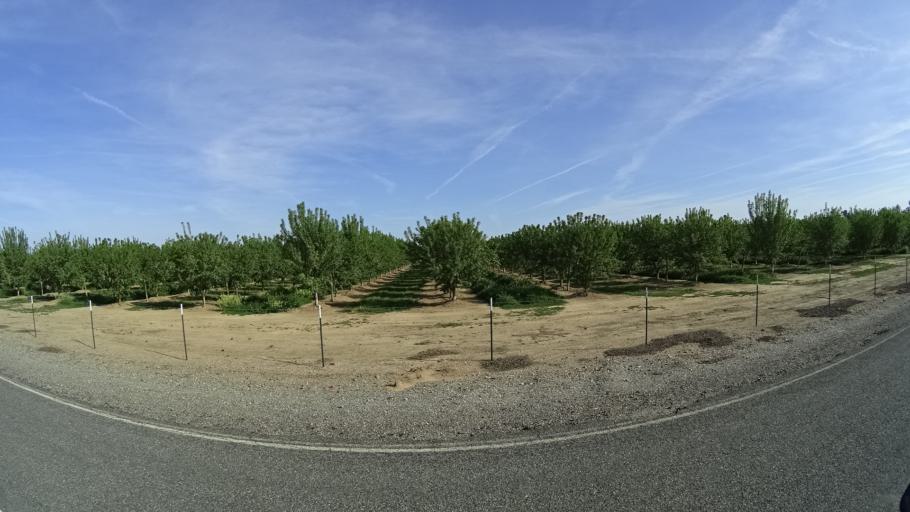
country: US
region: California
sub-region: Glenn County
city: Orland
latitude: 39.6680
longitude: -122.2226
